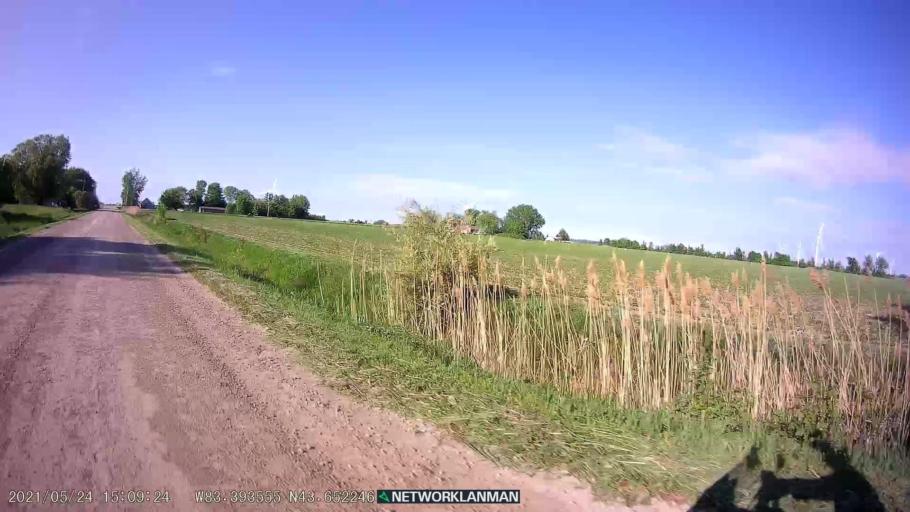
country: US
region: Michigan
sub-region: Huron County
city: Sebewaing
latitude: 43.6527
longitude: -83.3936
